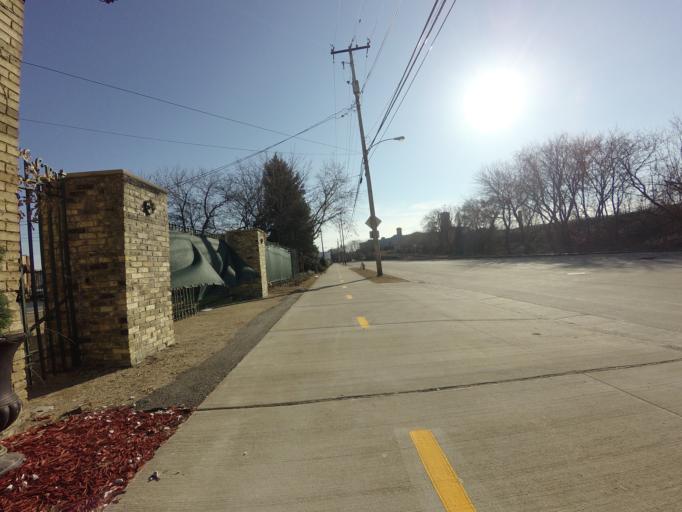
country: US
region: Wisconsin
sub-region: Milwaukee County
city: Milwaukee
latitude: 43.0227
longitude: -87.9067
